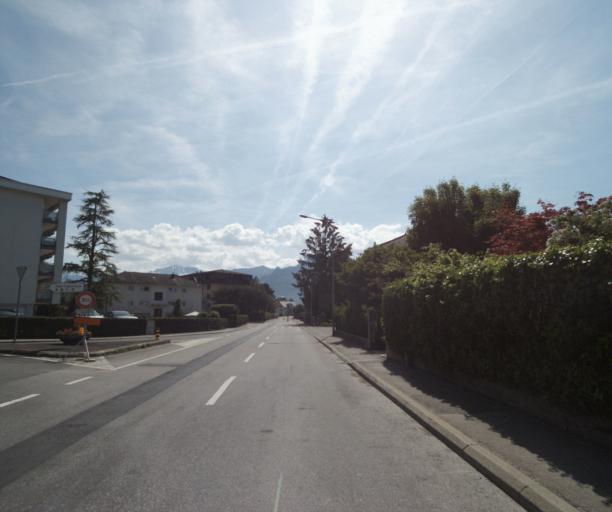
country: CH
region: Vaud
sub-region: Aigle District
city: Villeneuve
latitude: 46.3956
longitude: 6.9259
